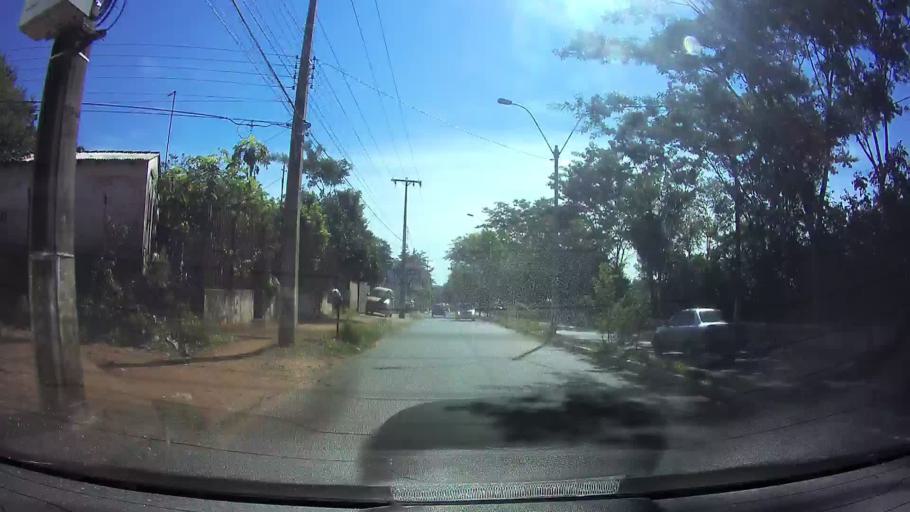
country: PY
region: Central
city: Villa Elisa
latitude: -25.3696
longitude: -57.5787
